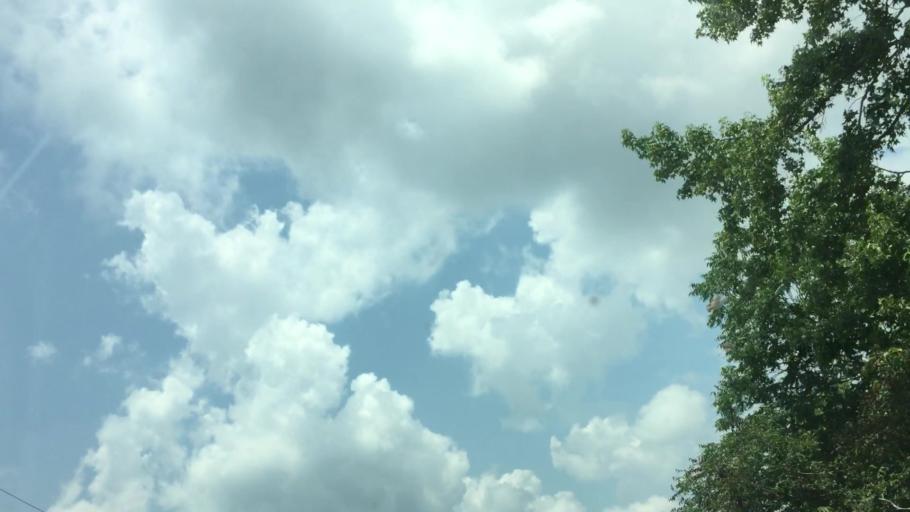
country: US
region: Georgia
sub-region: Carroll County
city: Villa Rica
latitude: 33.6102
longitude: -84.9317
